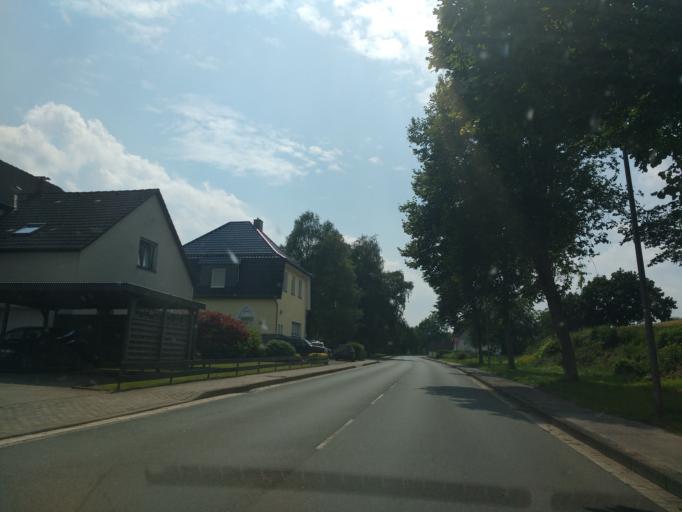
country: DE
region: North Rhine-Westphalia
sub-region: Regierungsbezirk Detmold
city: Dorentrup
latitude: 52.0828
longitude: 9.0074
